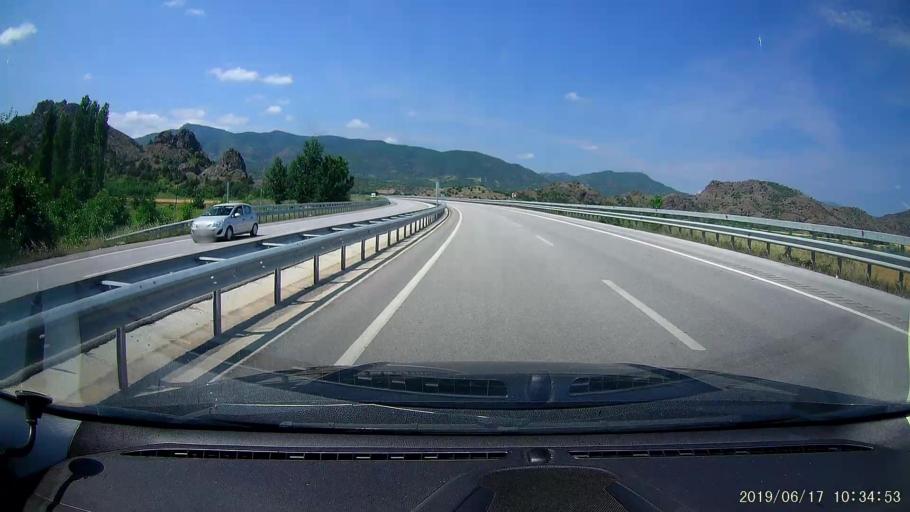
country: TR
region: Corum
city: Osmancik
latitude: 40.9804
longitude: 34.7144
